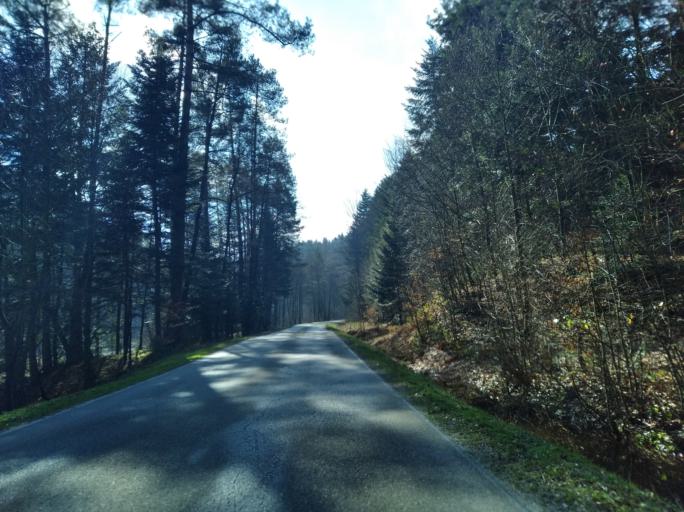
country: PL
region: Subcarpathian Voivodeship
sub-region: Powiat strzyzowski
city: Frysztak
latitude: 49.8653
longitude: 21.5506
